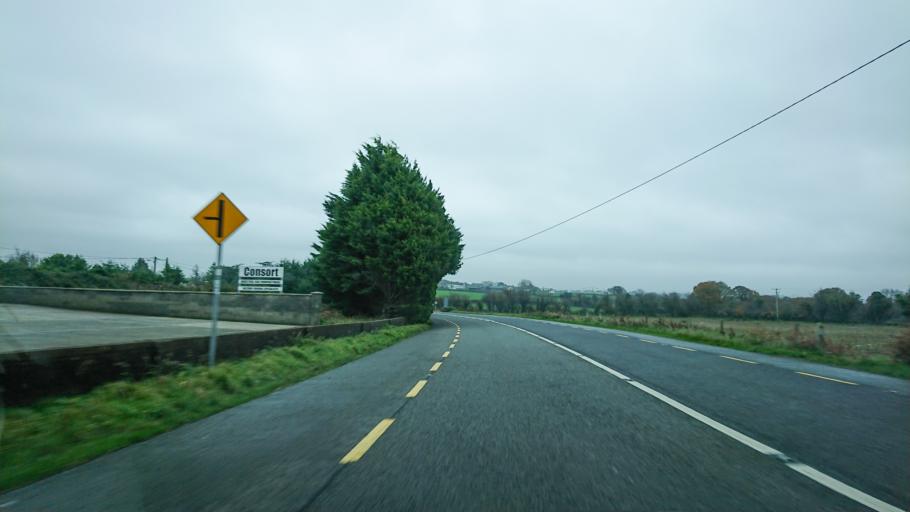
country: IE
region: Leinster
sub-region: Kilkenny
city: Mooncoin
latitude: 52.2905
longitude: -7.2423
